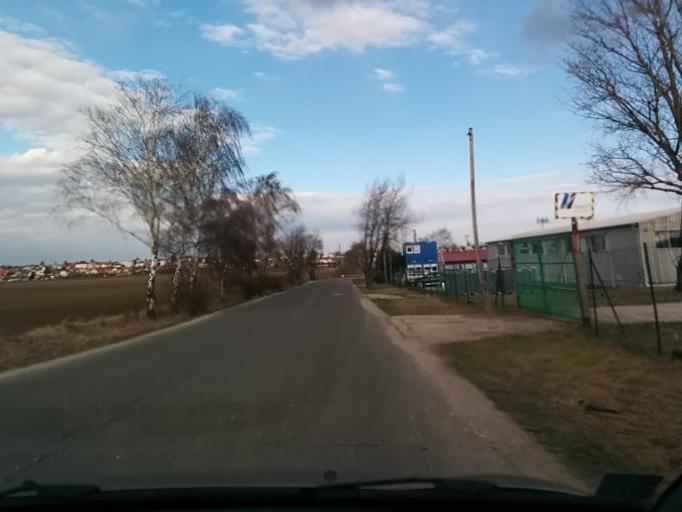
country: SK
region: Trnavsky
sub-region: Okres Trnava
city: Trnava
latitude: 48.3415
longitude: 17.6051
